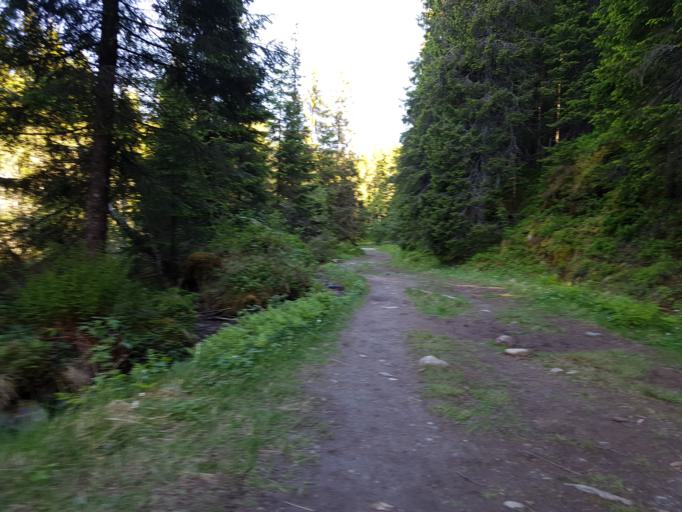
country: NO
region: Sor-Trondelag
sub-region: Trondheim
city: Trondheim
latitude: 63.4173
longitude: 10.3273
